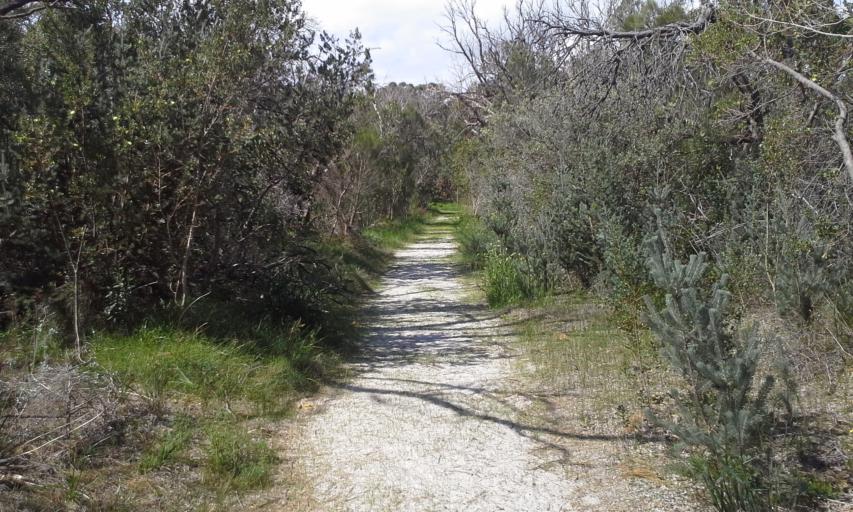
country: AU
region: Western Australia
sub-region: City of Perth
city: West Perth
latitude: -31.9615
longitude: 115.8374
